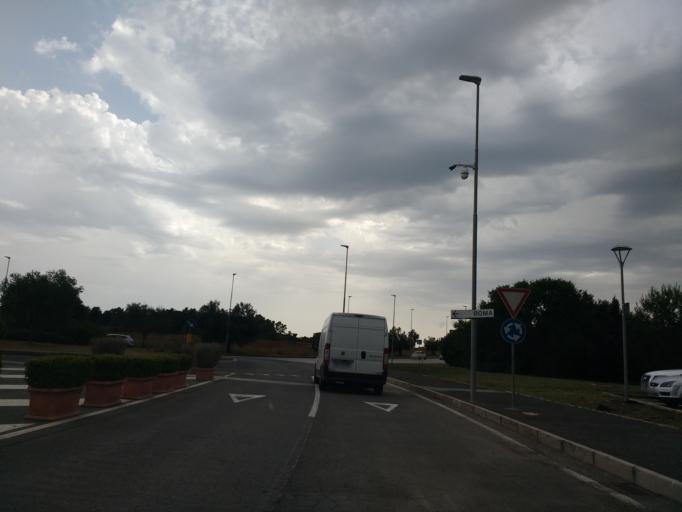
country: IT
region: Latium
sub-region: Citta metropolitana di Roma Capitale
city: Monte Migliore-La Selvotta
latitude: 41.7149
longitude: 12.4436
